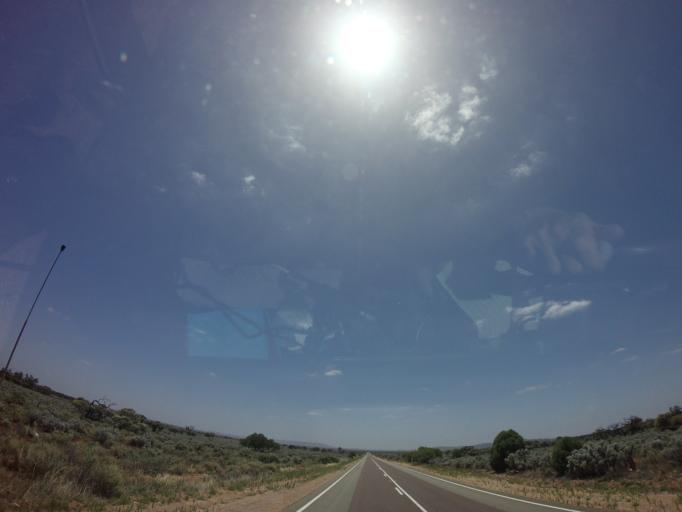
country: AU
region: South Australia
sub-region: Whyalla
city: Whyalla
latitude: -32.8166
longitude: 137.0451
